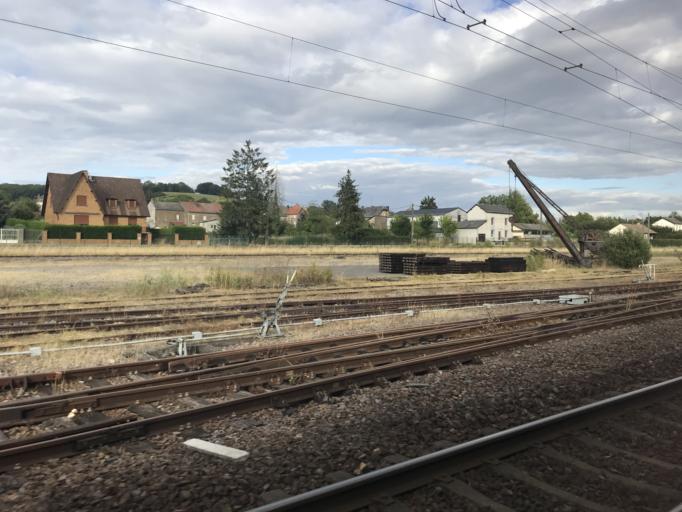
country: FR
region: Champagne-Ardenne
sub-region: Departement des Ardennes
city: Carignan
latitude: 49.6277
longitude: 5.1698
